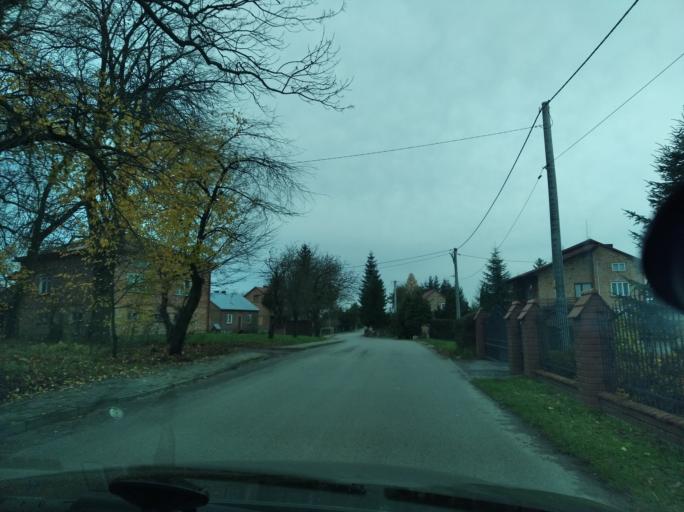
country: PL
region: Subcarpathian Voivodeship
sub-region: Powiat przeworski
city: Debow
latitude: 50.0455
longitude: 22.4319
